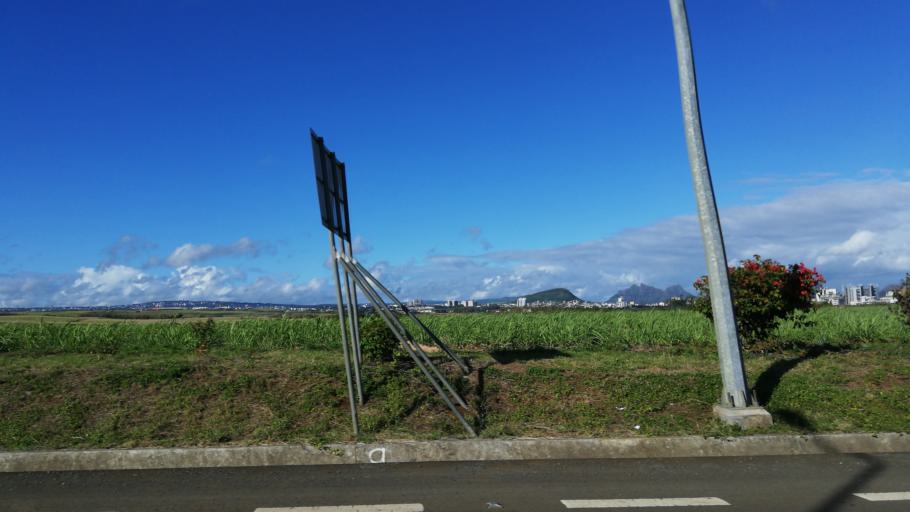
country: MU
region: Moka
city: Moka
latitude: -20.2331
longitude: 57.5066
